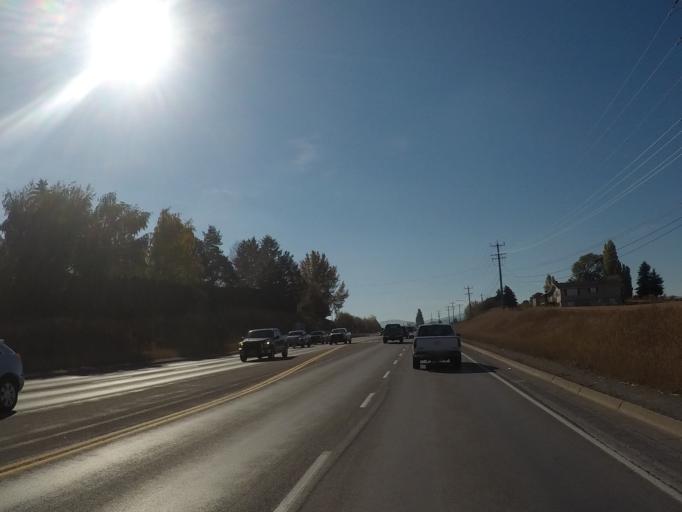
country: US
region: Montana
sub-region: Flathead County
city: Kalispell
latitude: 48.2245
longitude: -114.3307
